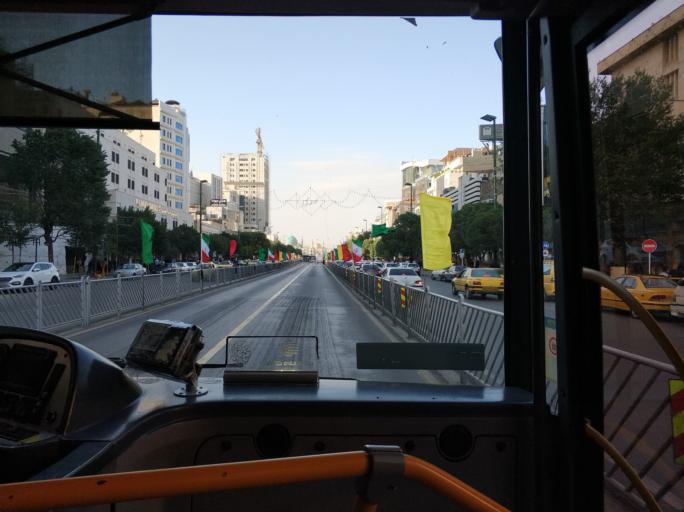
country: IR
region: Razavi Khorasan
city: Mashhad
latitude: 36.2806
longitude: 59.6095
